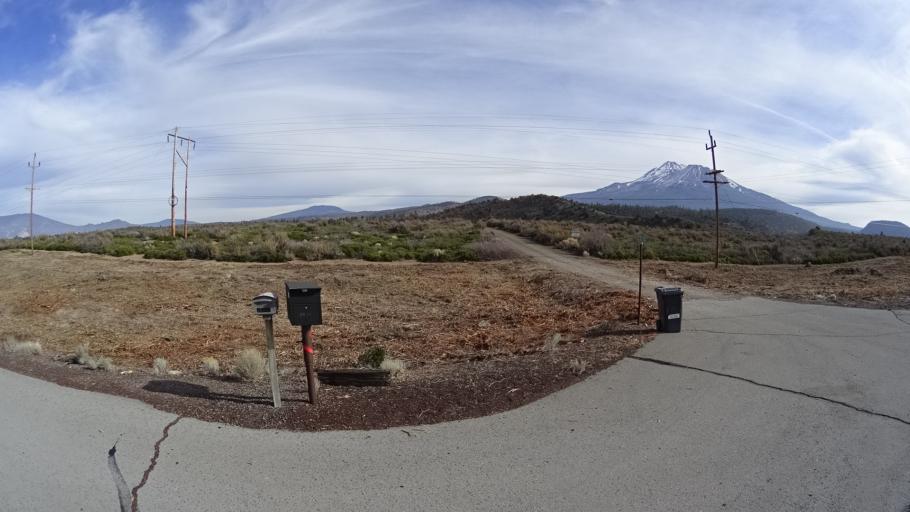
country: US
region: California
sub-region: Siskiyou County
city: Weed
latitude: 41.4832
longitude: -122.3622
